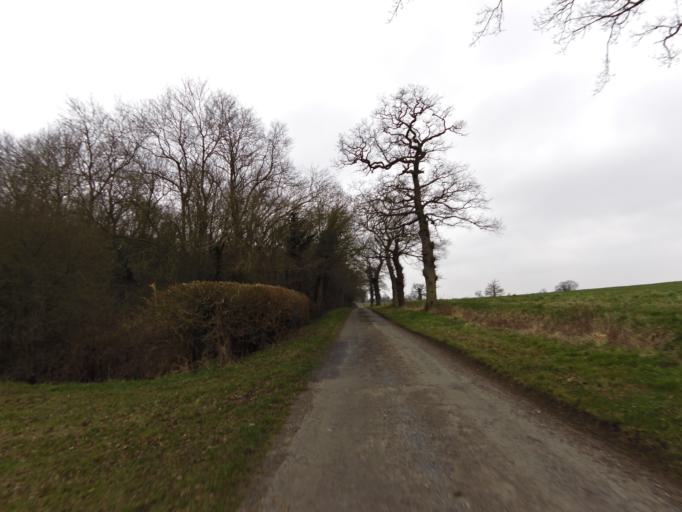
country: GB
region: England
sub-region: Suffolk
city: Framlingham
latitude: 52.2377
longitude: 1.3892
